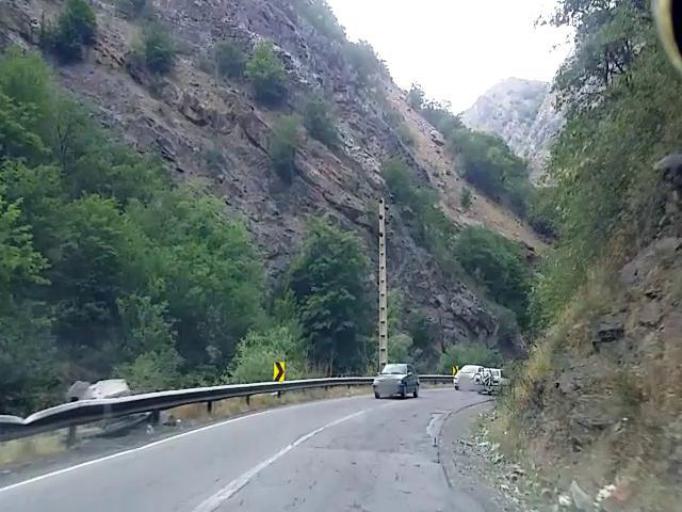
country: IR
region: Mazandaran
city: Chalus
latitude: 36.2836
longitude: 51.2419
